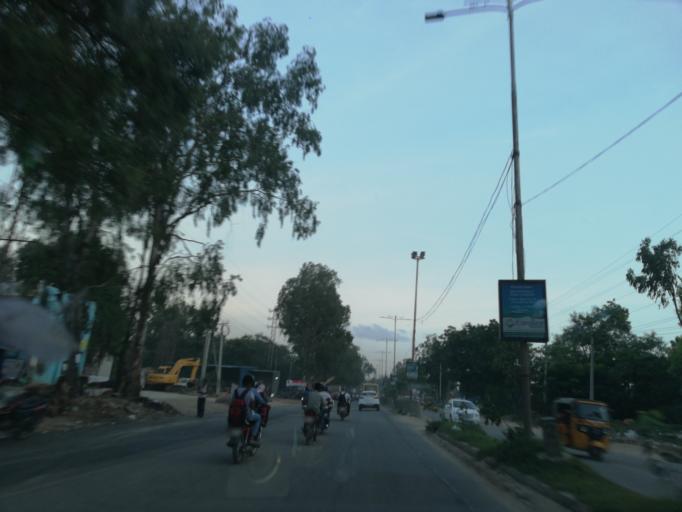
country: IN
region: Telangana
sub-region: Medak
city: Serilingampalle
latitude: 17.5249
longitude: 78.3553
